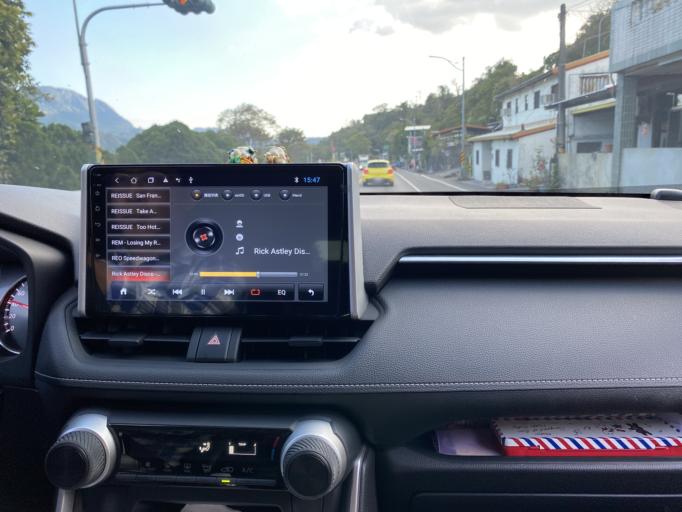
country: TW
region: Taiwan
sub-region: Taitung
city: Taitung
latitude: 22.9091
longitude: 121.1361
